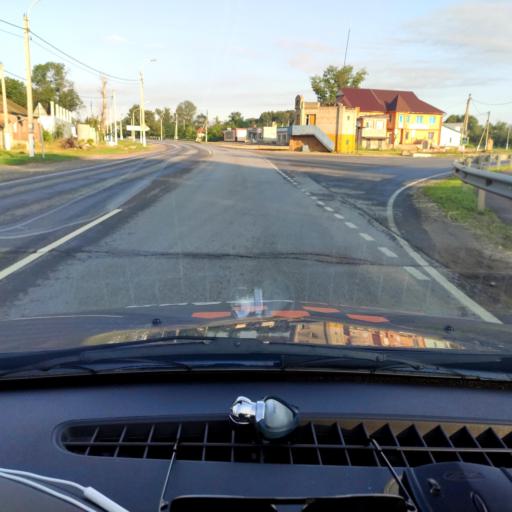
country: RU
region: Lipetsk
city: Kazaki
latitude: 52.5685
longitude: 38.1862
